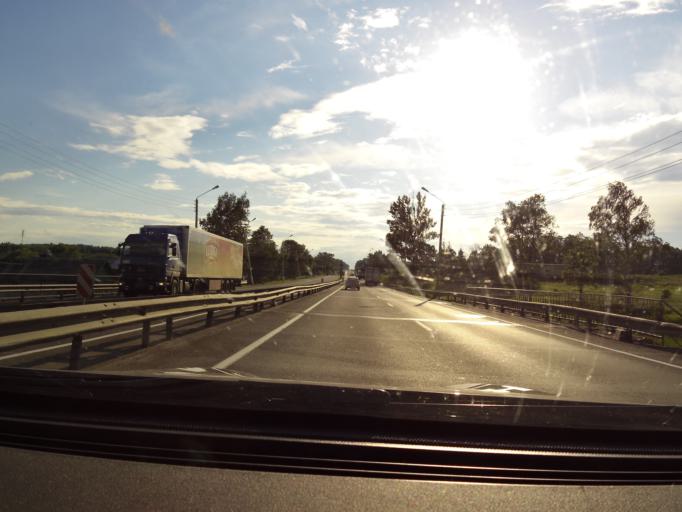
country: RU
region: Vladimir
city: Melekhovo
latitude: 56.2104
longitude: 41.2860
